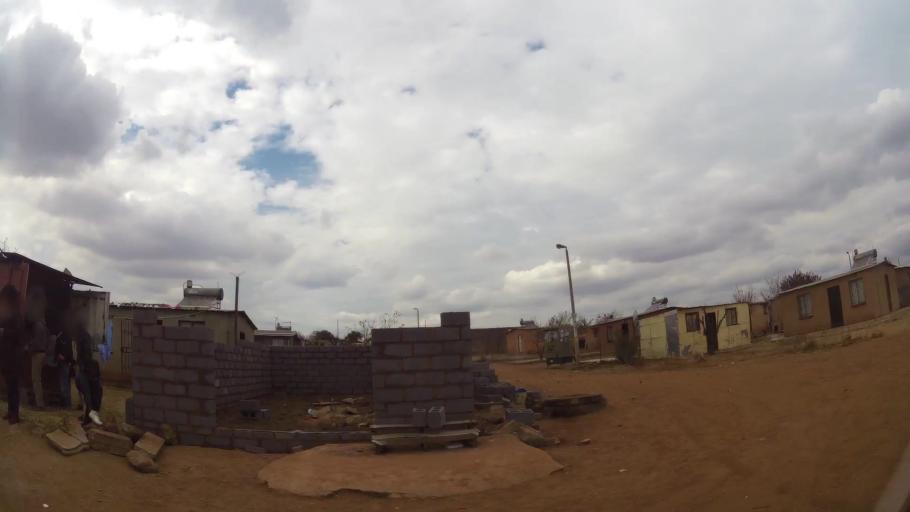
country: ZA
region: Gauteng
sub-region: Ekurhuleni Metropolitan Municipality
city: Germiston
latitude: -26.3764
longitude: 28.1173
